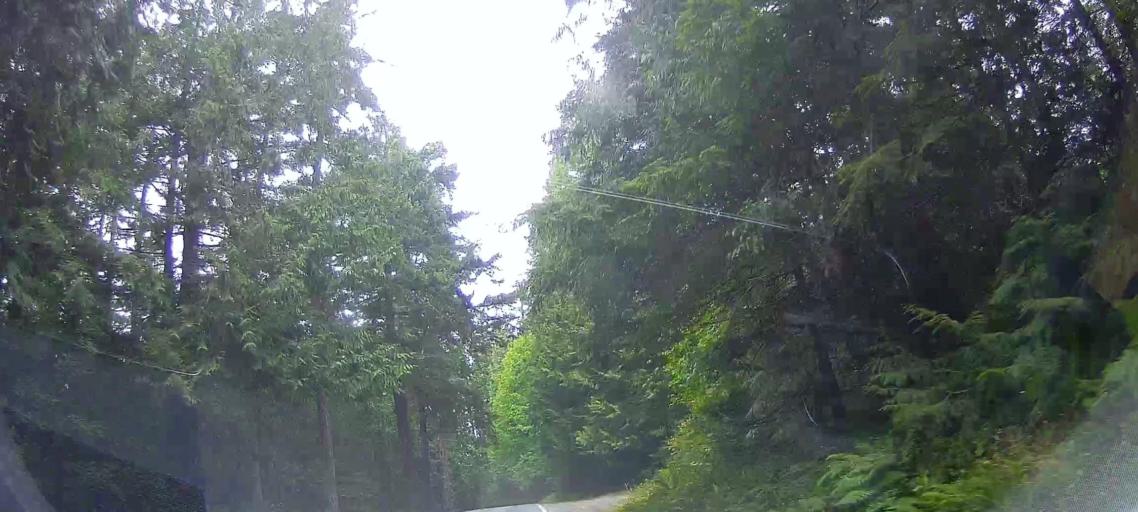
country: US
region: Washington
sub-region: Skagit County
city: Anacortes
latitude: 48.4792
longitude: -122.6262
